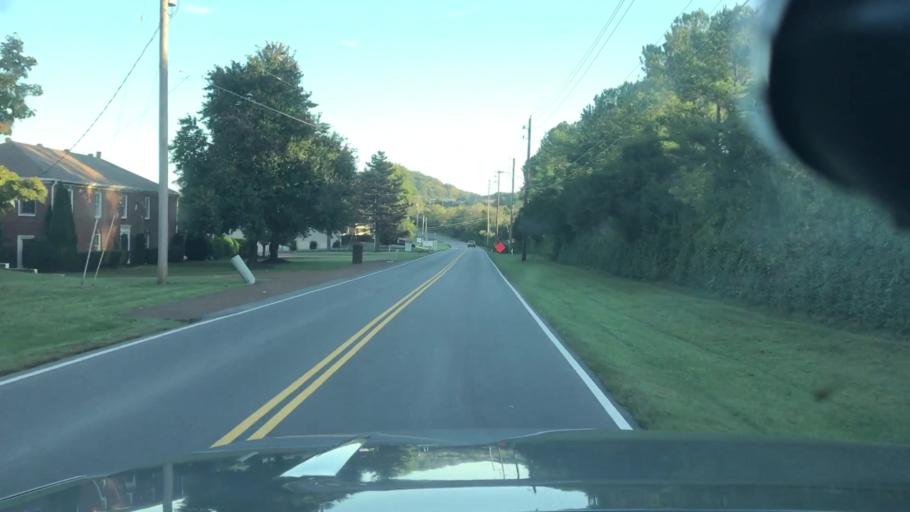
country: US
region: Tennessee
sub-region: Williamson County
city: Brentwood Estates
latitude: 36.0251
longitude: -86.7861
